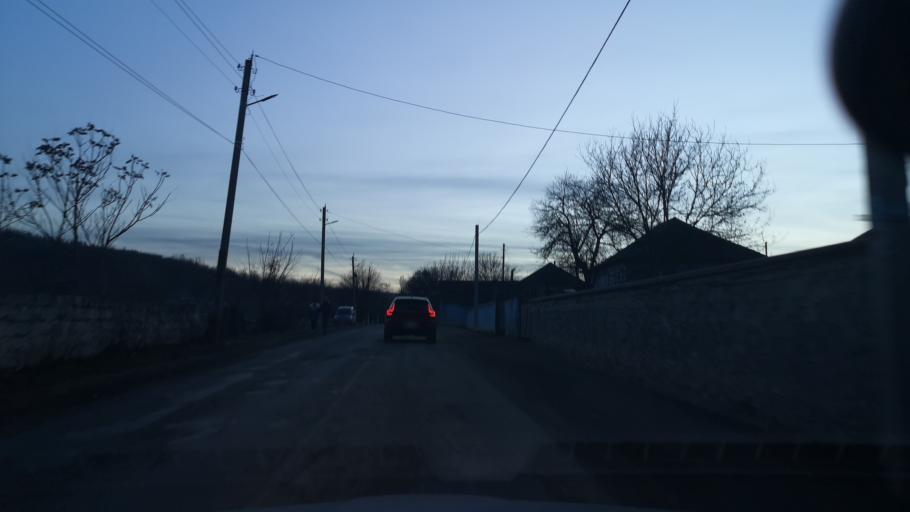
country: MD
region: Orhei
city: Orhei
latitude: 47.3048
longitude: 28.9234
